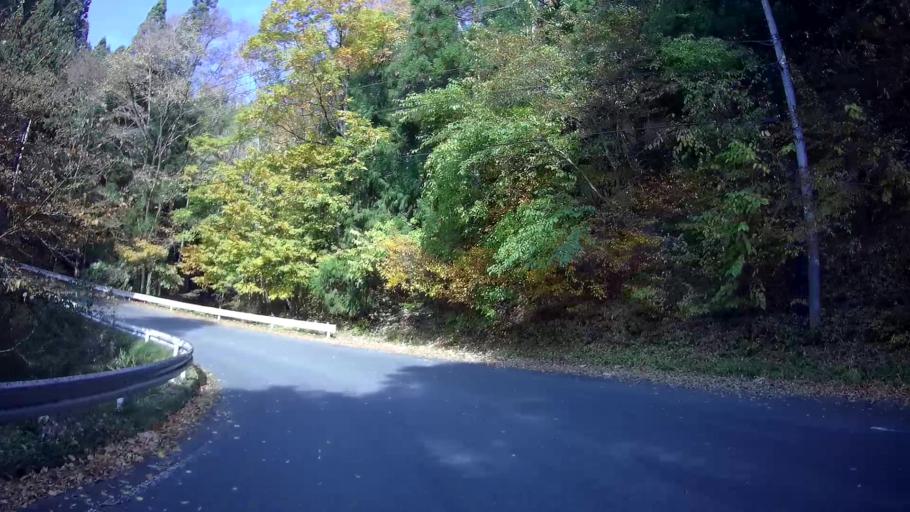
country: JP
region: Gunma
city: Nakanojomachi
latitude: 36.5098
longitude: 138.6756
